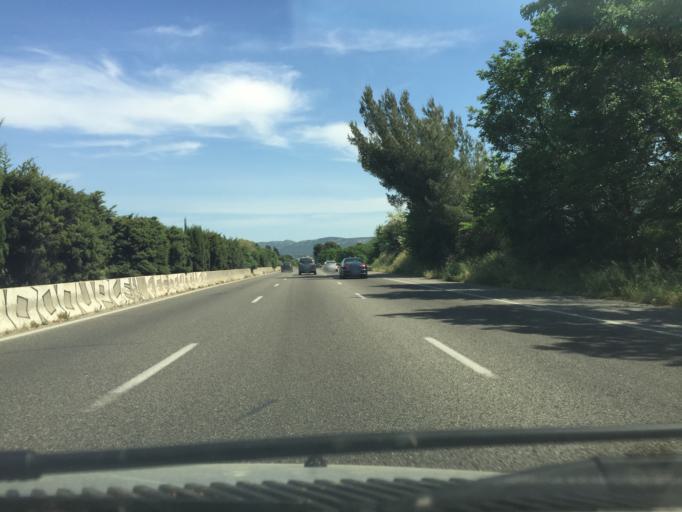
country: FR
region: Provence-Alpes-Cote d'Azur
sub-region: Departement des Bouches-du-Rhone
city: La Penne-sur-Huveaune
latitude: 43.2901
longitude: 5.4902
